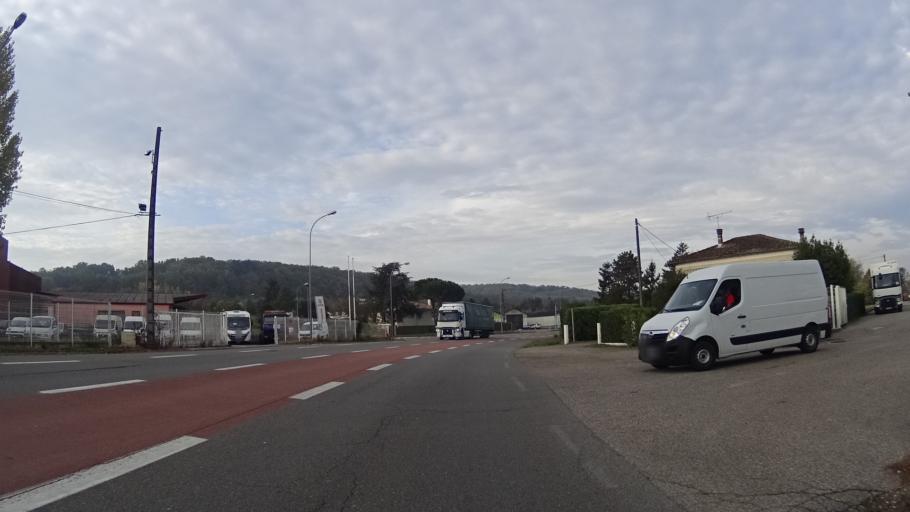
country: FR
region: Aquitaine
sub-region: Departement du Lot-et-Garonne
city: Boe
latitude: 44.1649
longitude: 0.6023
